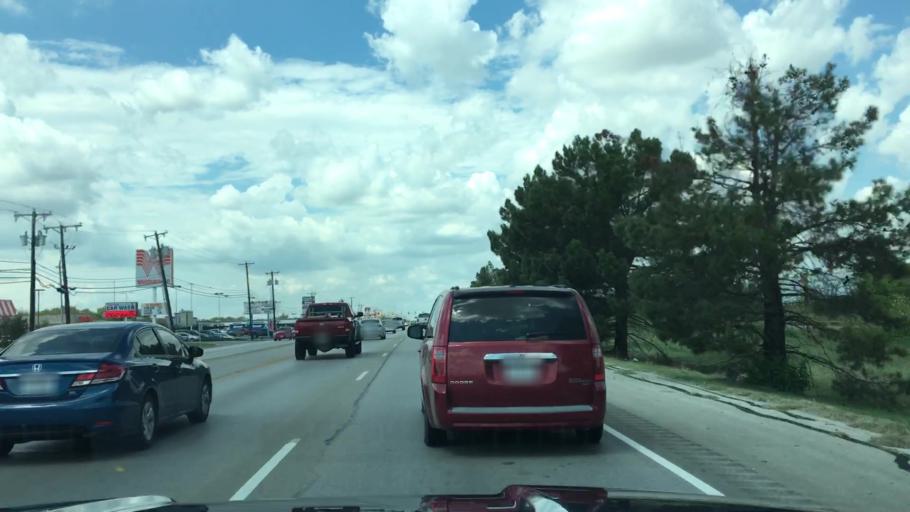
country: US
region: Texas
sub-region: Tarrant County
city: Saginaw
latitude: 32.8743
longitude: -97.3759
